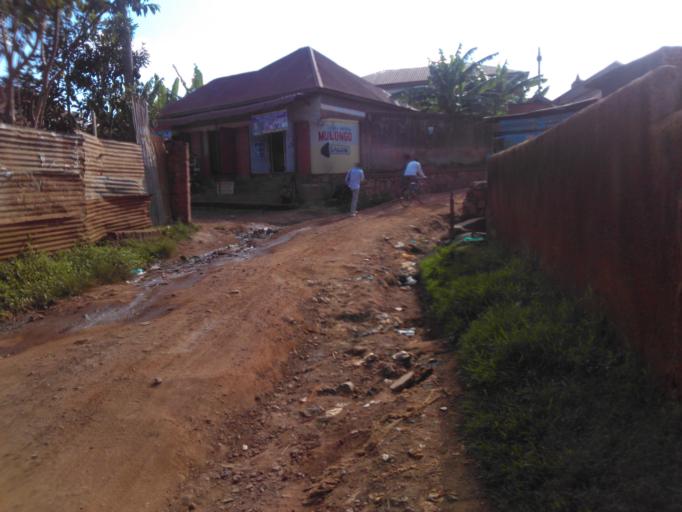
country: UG
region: Central Region
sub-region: Wakiso District
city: Kajansi
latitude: 0.2530
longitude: 32.5643
